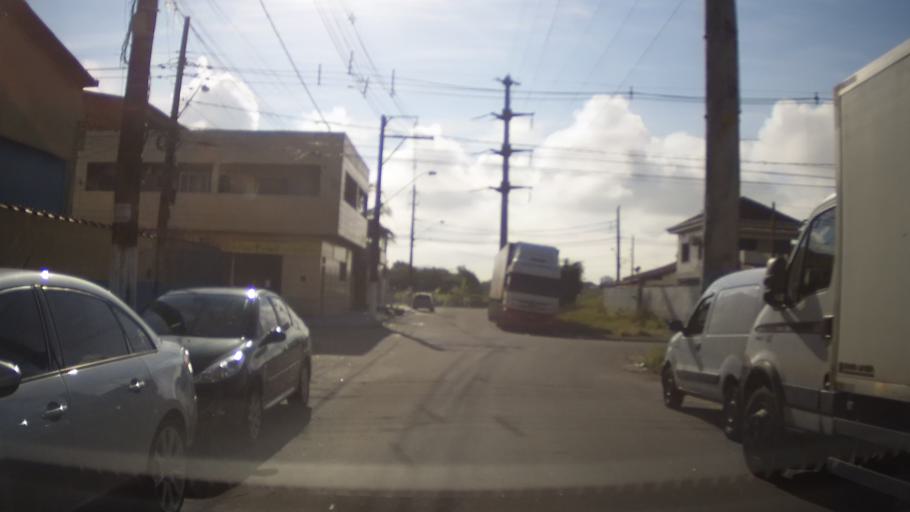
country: BR
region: Sao Paulo
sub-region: Praia Grande
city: Praia Grande
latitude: -24.0150
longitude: -46.4759
